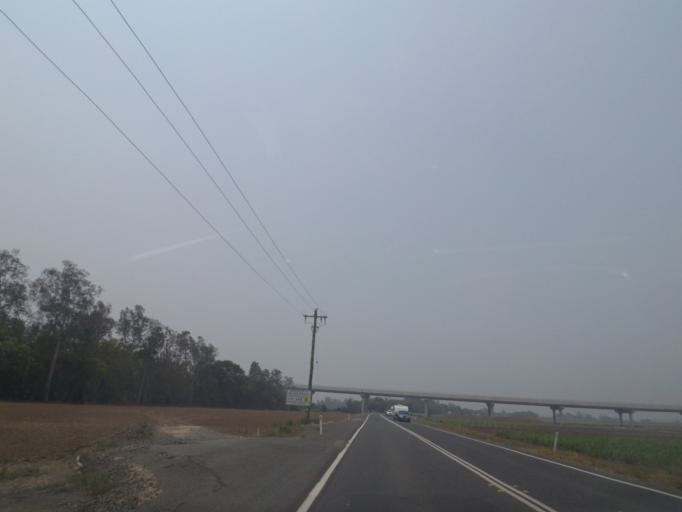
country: AU
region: New South Wales
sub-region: Richmond Valley
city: Evans Head
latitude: -29.0006
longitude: 153.4389
